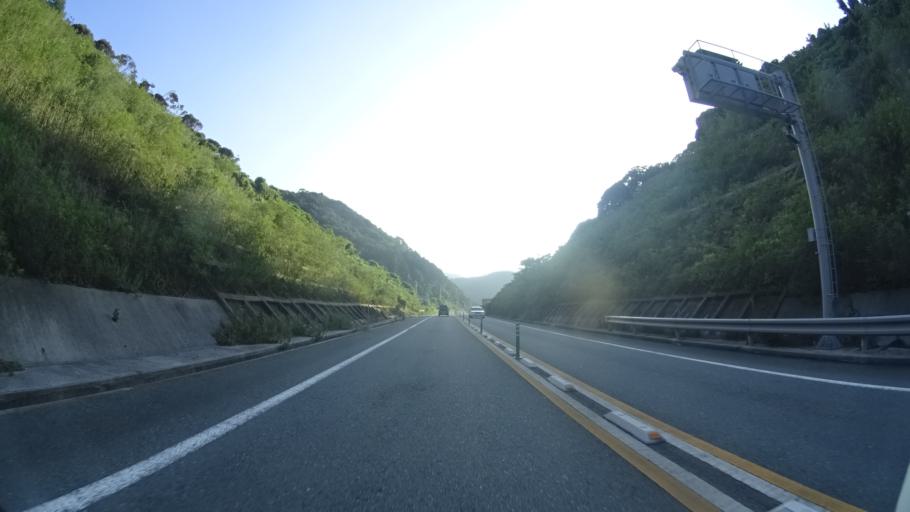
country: JP
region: Yamaguchi
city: Nagato
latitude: 34.3804
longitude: 131.3084
